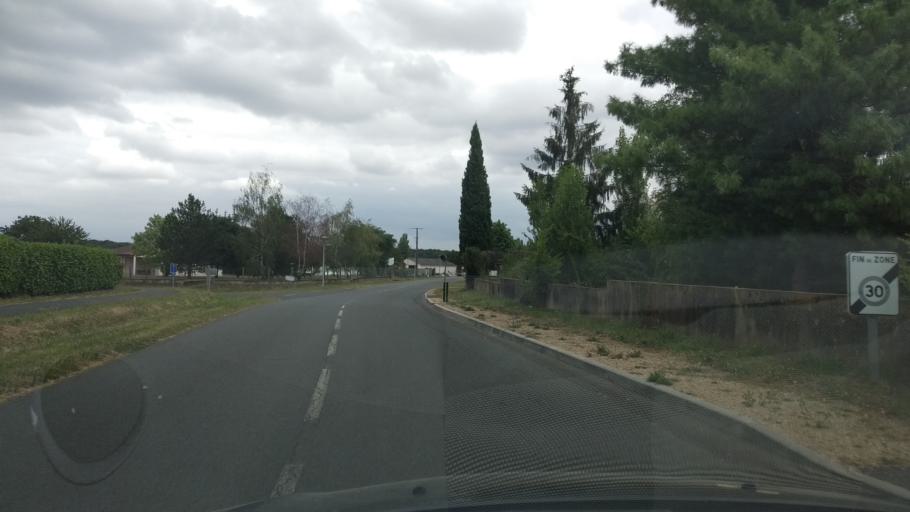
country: FR
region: Poitou-Charentes
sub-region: Departement de la Vienne
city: Smarves
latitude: 46.5076
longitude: 0.3580
